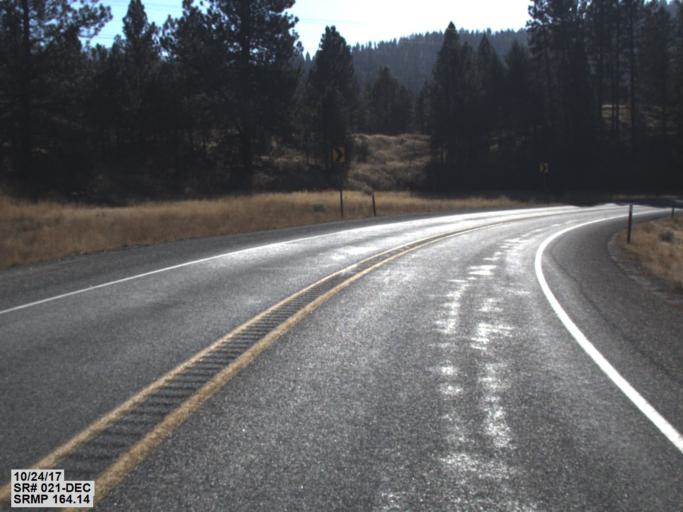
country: US
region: Washington
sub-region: Ferry County
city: Republic
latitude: 48.6622
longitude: -118.6657
